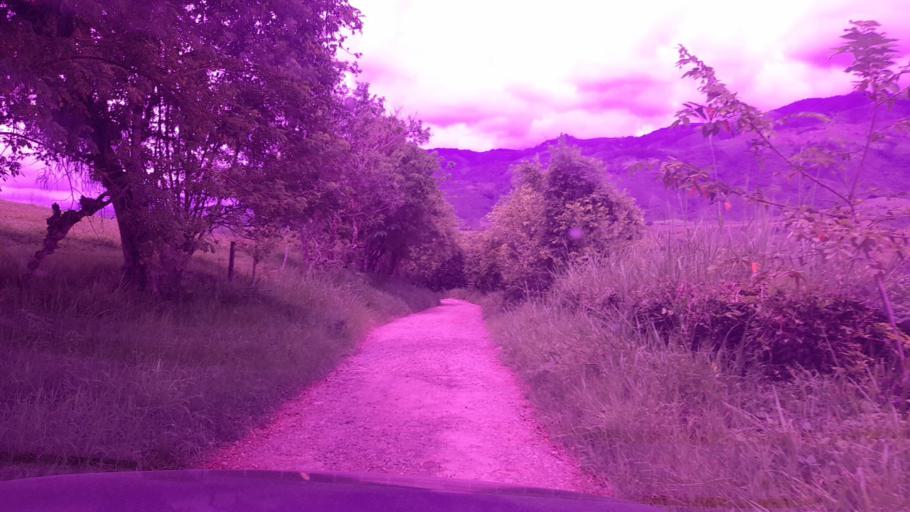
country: CO
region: Valle del Cauca
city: Andalucia
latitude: 4.1657
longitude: -76.0917
